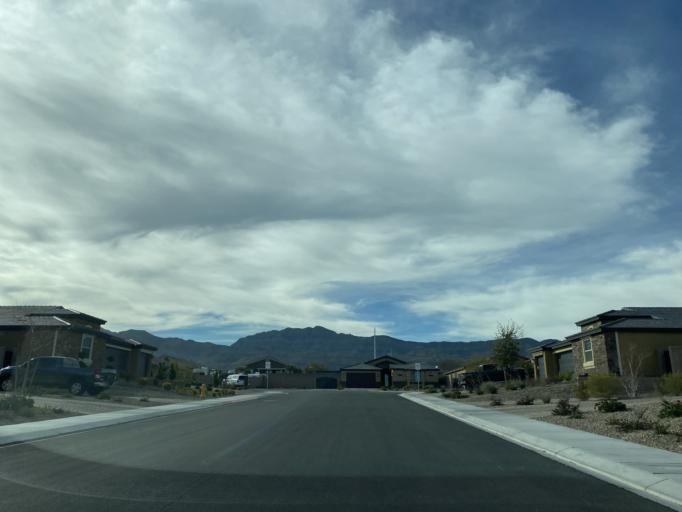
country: US
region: Nevada
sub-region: Clark County
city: Summerlin South
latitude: 36.2694
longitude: -115.3251
